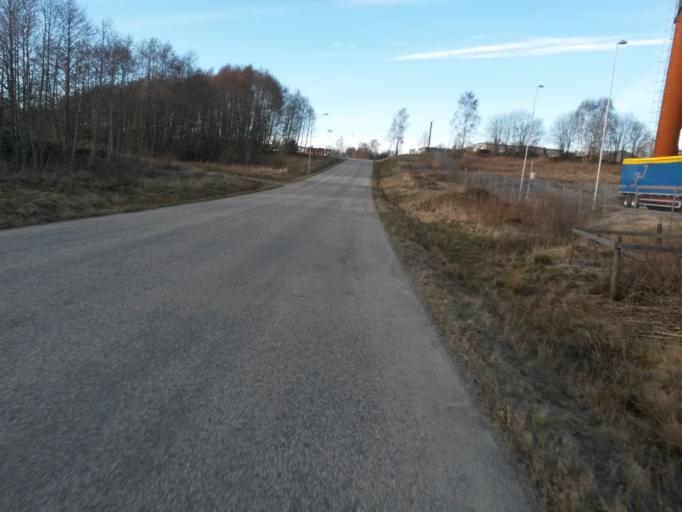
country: SE
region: Vaestra Goetaland
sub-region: Vargarda Kommun
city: Vargarda
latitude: 58.0264
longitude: 12.7913
